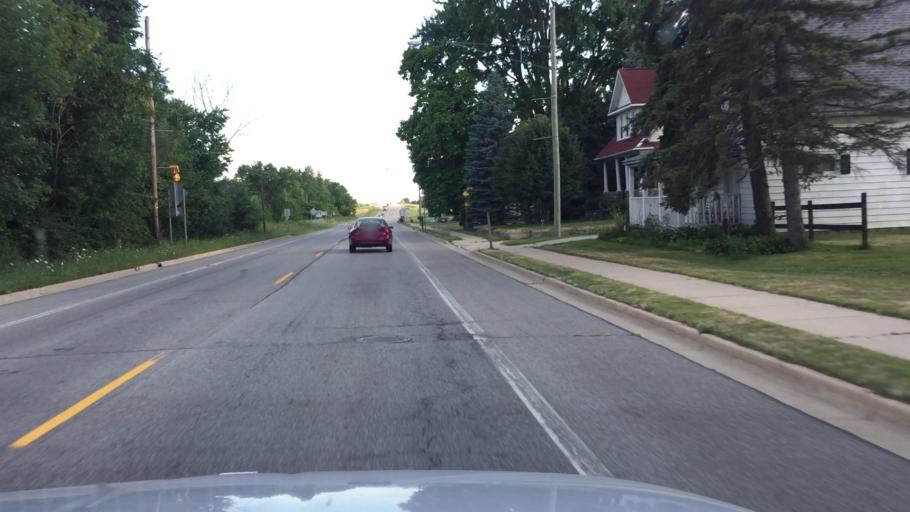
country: US
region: Michigan
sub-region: Macomb County
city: Memphis
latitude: 42.9884
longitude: -82.7651
